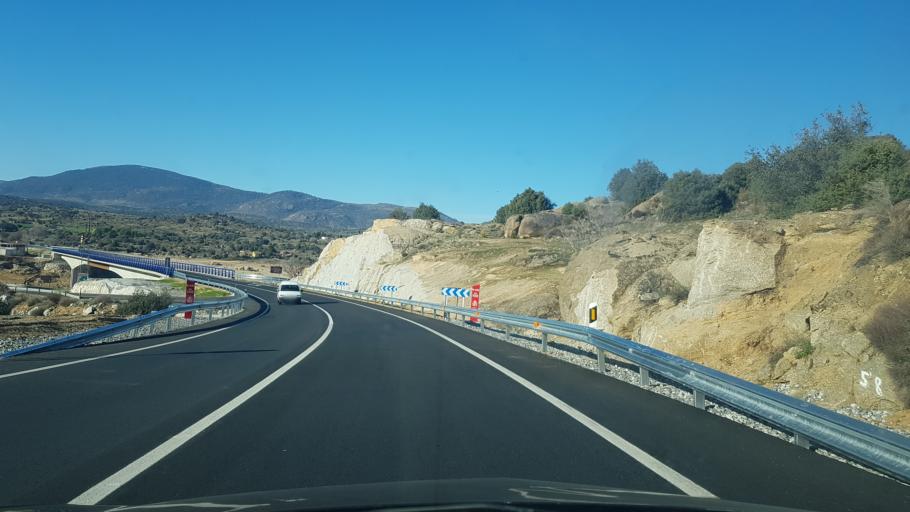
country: ES
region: Castille and Leon
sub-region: Provincia de Avila
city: El Tiemblo
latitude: 40.4417
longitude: -4.5614
